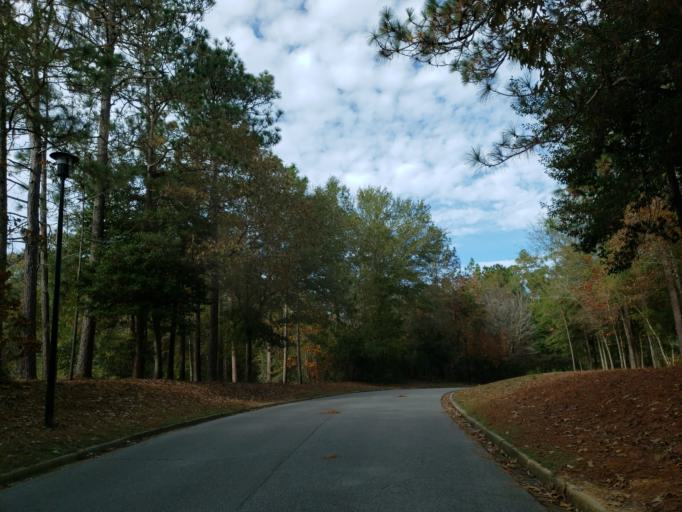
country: US
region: Mississippi
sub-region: Lamar County
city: West Hattiesburg
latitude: 31.3198
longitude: -89.4722
